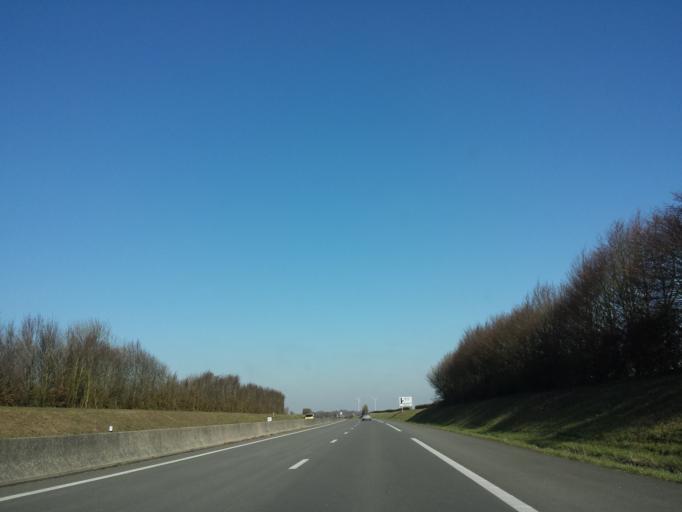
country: FR
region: Picardie
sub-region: Departement de la Somme
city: Conty
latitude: 49.7154
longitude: 2.2403
